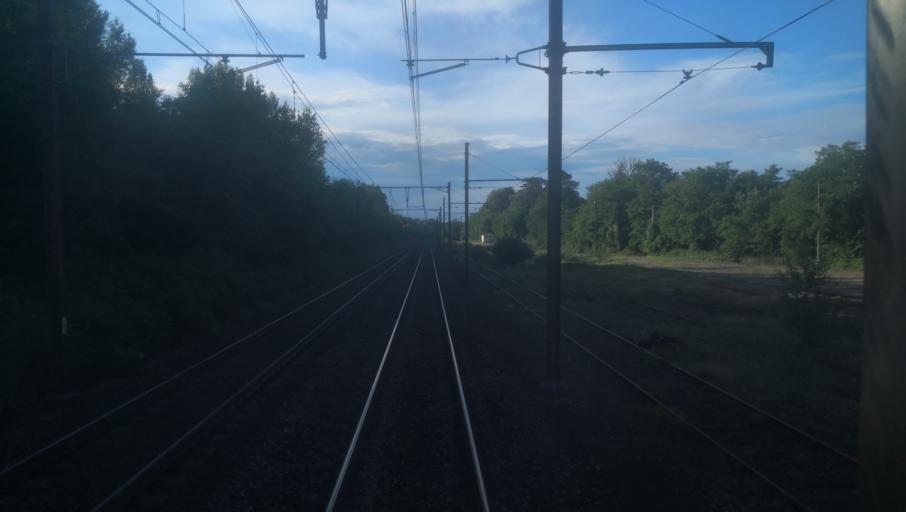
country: FR
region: Centre
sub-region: Departement du Cher
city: Vierzon
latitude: 47.2464
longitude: 2.0452
